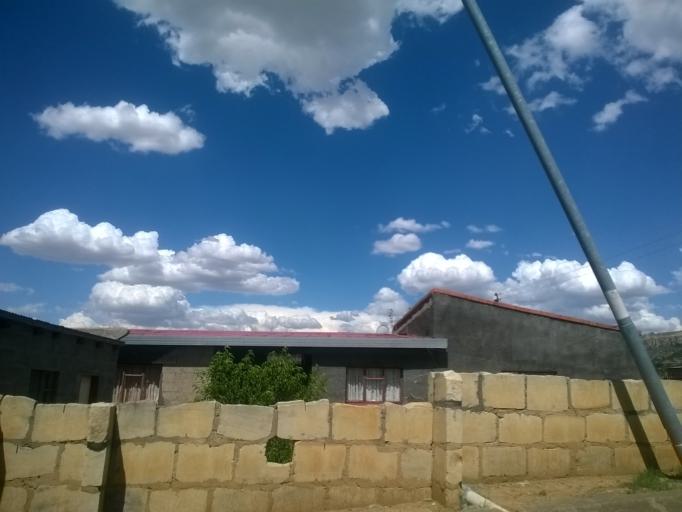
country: LS
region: Maseru
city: Maseru
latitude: -29.3193
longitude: 27.5107
